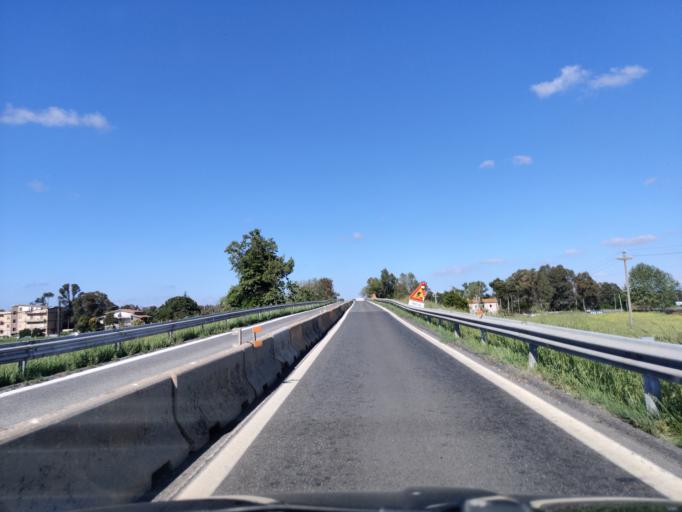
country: IT
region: Latium
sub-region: Citta metropolitana di Roma Capitale
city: Maccarese
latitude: 41.8868
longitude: 12.2261
